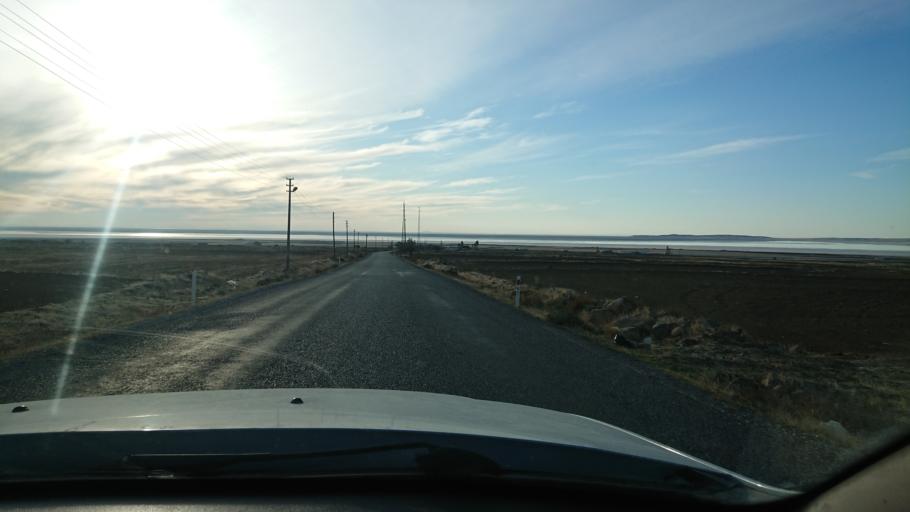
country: TR
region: Ankara
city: Sereflikochisar
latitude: 38.7441
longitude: 33.6767
